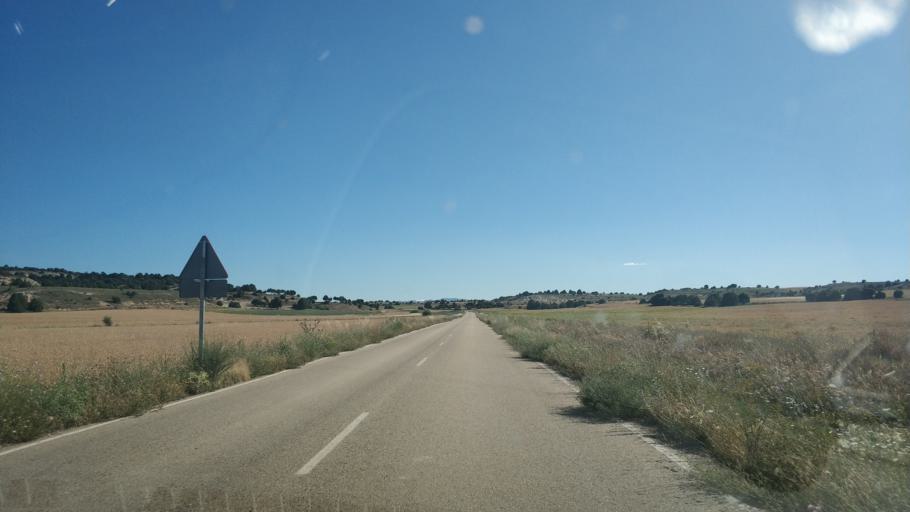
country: ES
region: Castille and Leon
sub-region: Provincia de Soria
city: San Esteban de Gormaz
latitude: 41.4840
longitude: -3.2111
